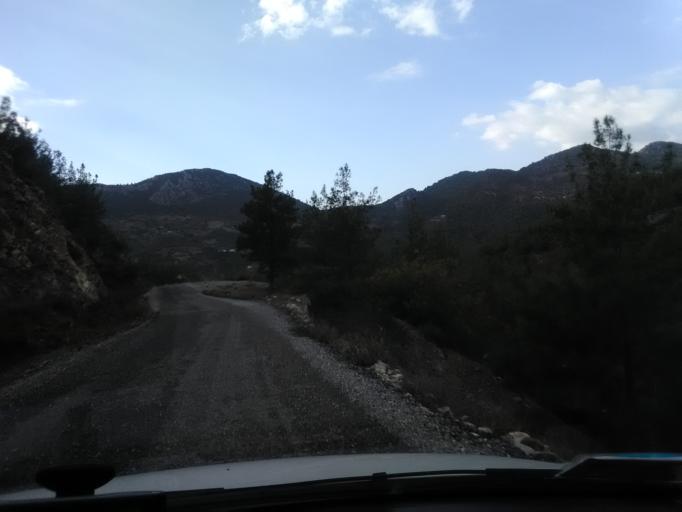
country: TR
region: Antalya
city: Gazipasa
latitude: 36.3032
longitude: 32.3886
